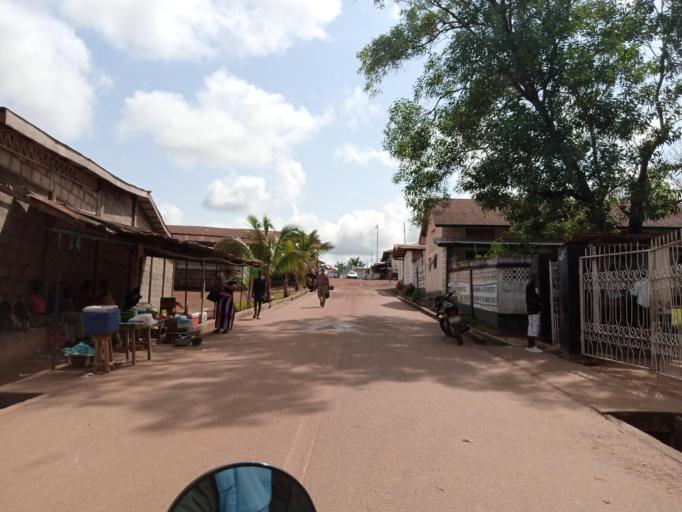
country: SL
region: Southern Province
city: Bo
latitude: 7.9712
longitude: -11.7346
